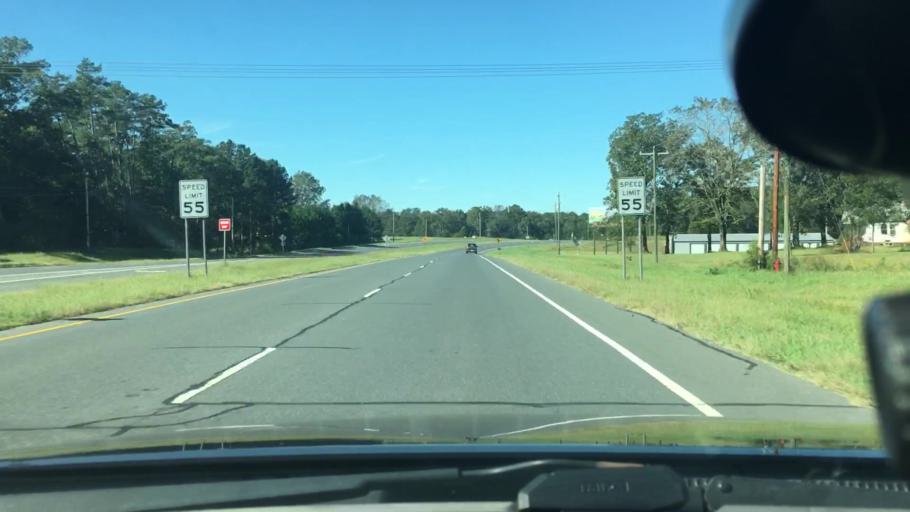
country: US
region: North Carolina
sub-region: Stanly County
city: Oakboro
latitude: 35.2733
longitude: -80.3162
